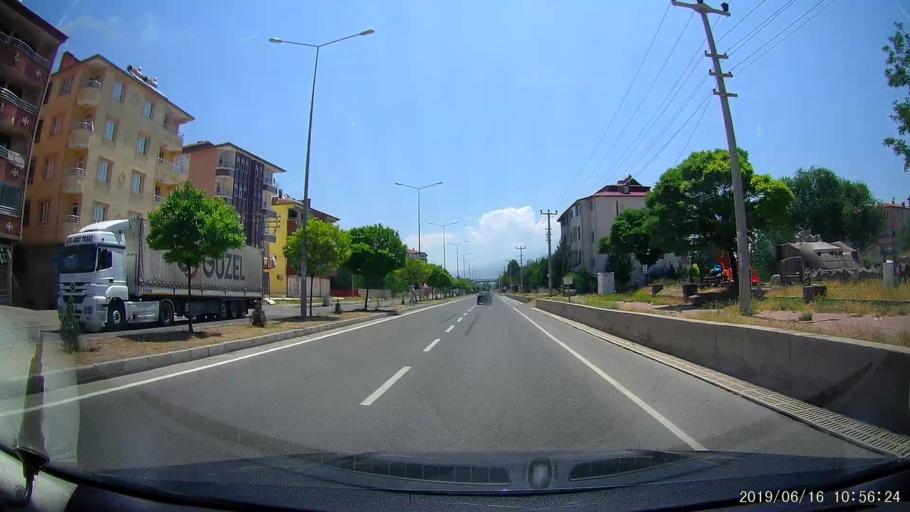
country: TR
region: Igdir
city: Igdir
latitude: 39.9302
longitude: 44.0215
